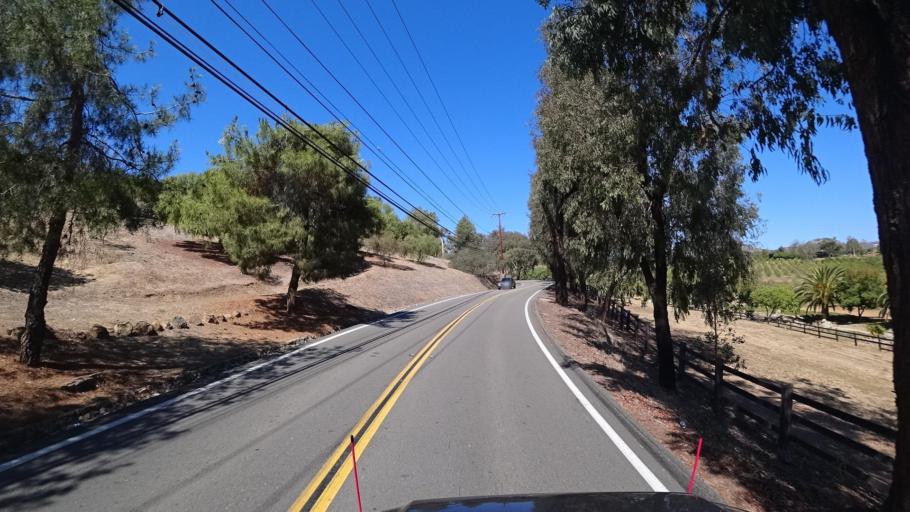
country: US
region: California
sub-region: San Diego County
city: Rancho Santa Fe
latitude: 33.0368
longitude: -117.1841
